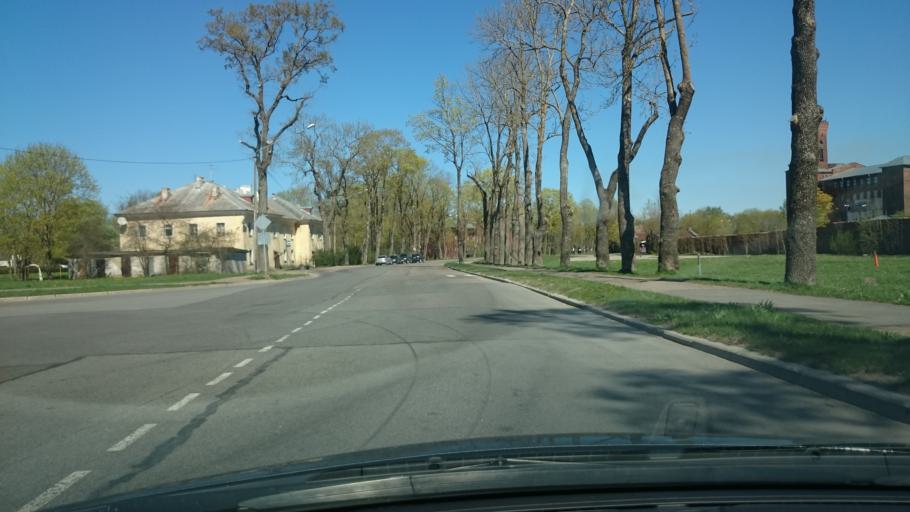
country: EE
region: Ida-Virumaa
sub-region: Narva linn
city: Narva
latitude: 59.3584
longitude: 28.1873
